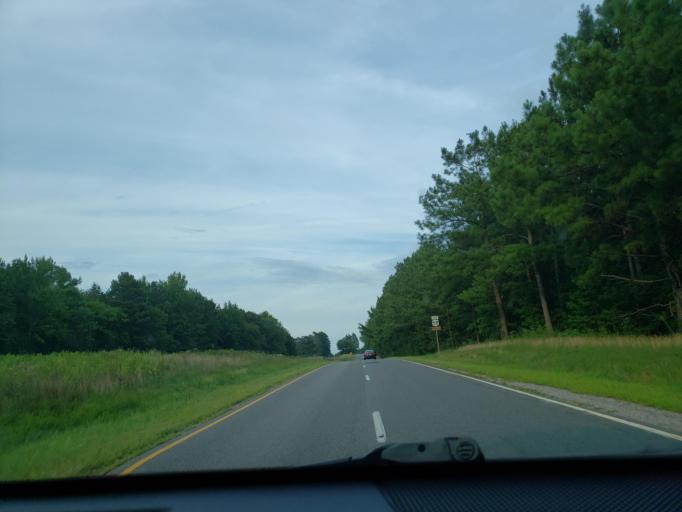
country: US
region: Virginia
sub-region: Brunswick County
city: Lawrenceville
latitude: 36.7434
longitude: -77.8853
